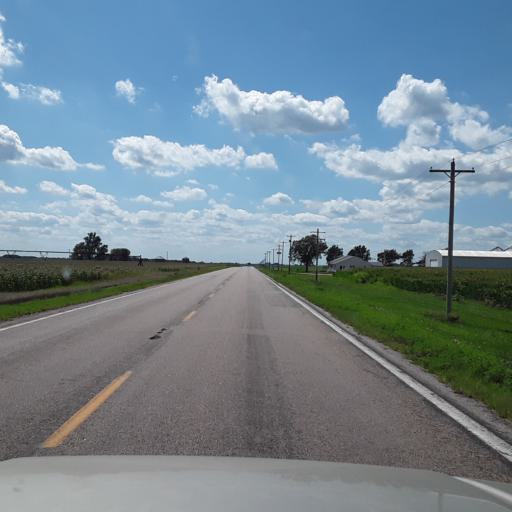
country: US
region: Nebraska
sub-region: Merrick County
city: Central City
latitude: 41.1911
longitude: -98.0329
